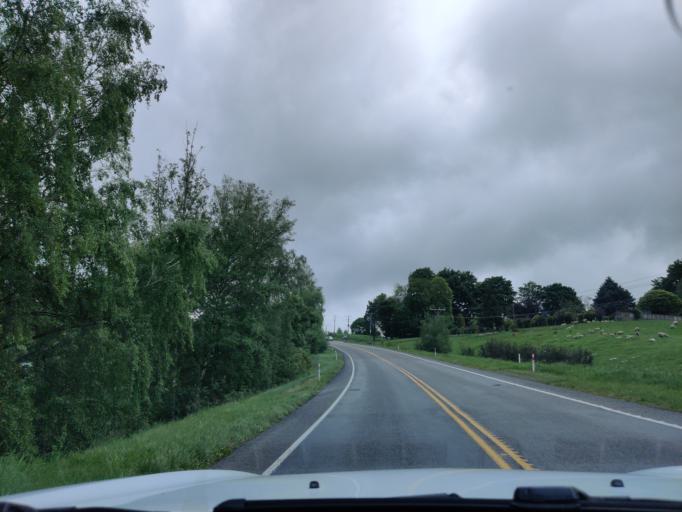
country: NZ
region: Manawatu-Wanganui
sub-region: Ruapehu District
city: Waiouru
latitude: -39.6567
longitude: 175.7787
